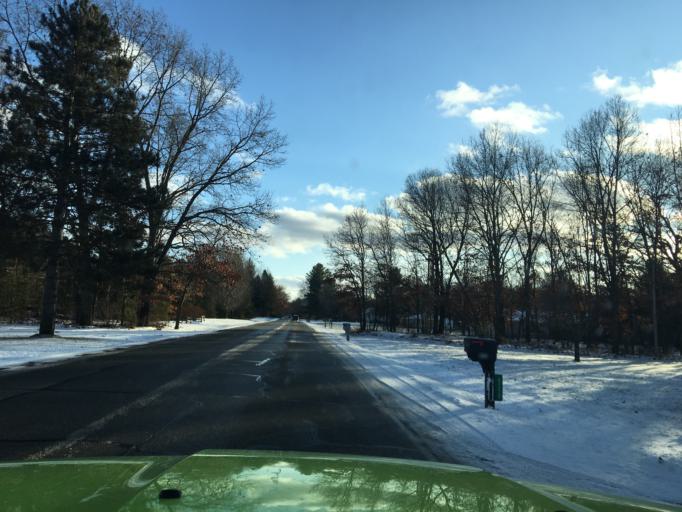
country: US
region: Michigan
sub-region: Montcalm County
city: Greenville
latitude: 43.2030
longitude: -85.2826
